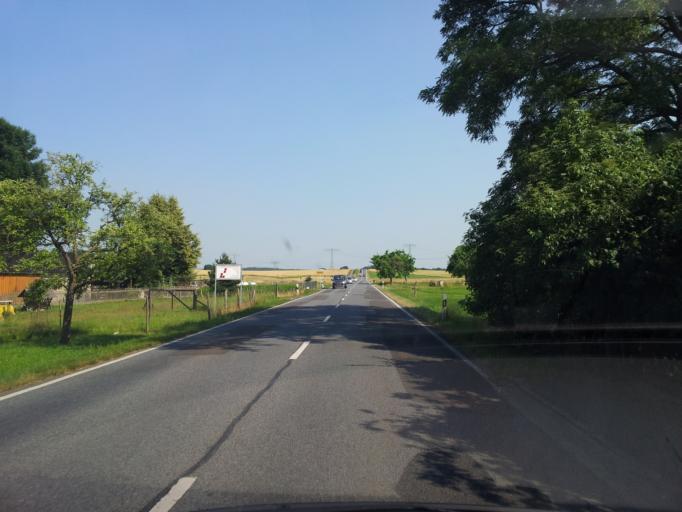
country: DE
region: Saxony
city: Wachau
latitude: 51.1571
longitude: 13.8855
